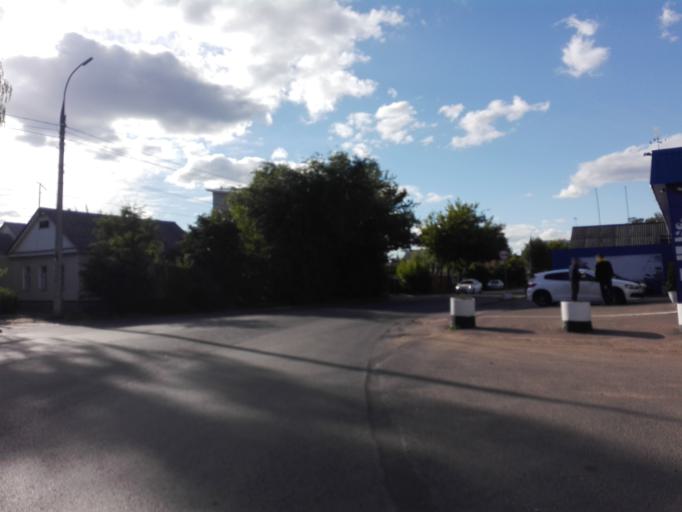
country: RU
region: Orjol
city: Orel
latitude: 52.9518
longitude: 36.0751
